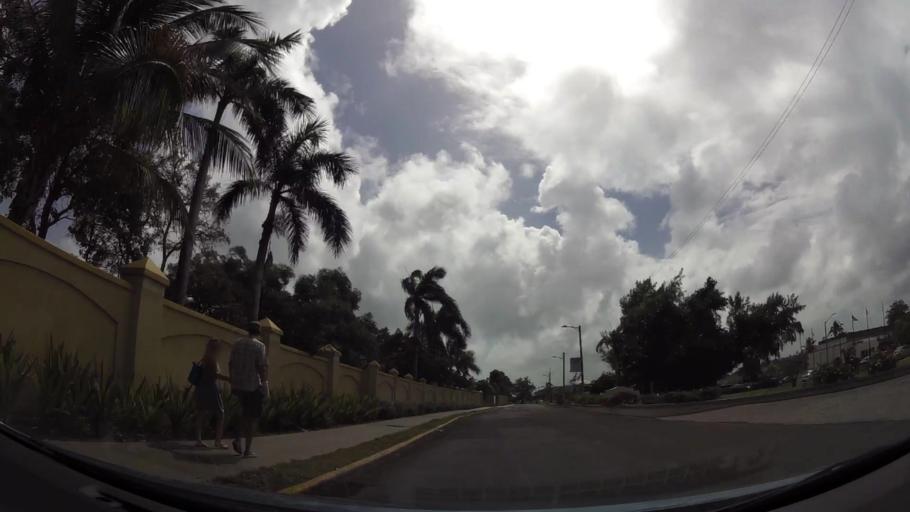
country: KN
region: Saint Peter Basseterre
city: Monkey Hill
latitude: 17.2911
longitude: -62.6858
